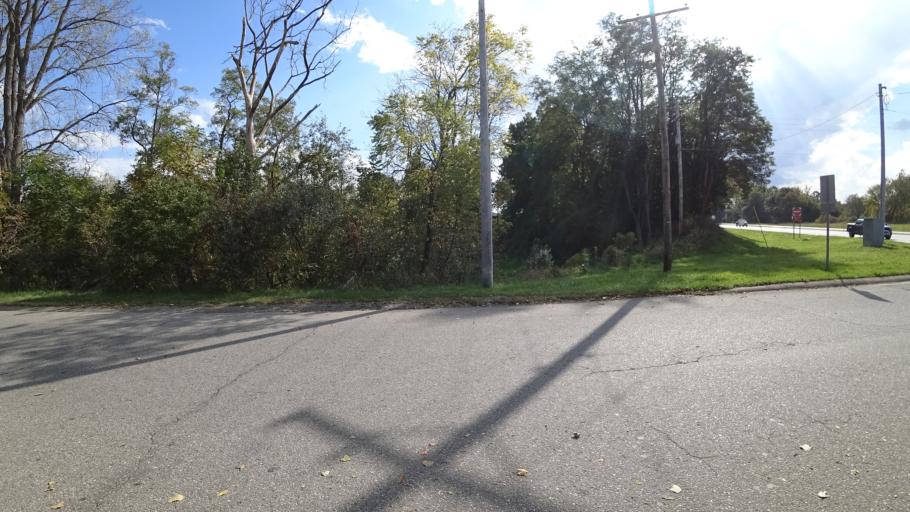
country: US
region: Michigan
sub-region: Saint Joseph County
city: Three Rivers
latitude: 41.9541
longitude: -85.6462
